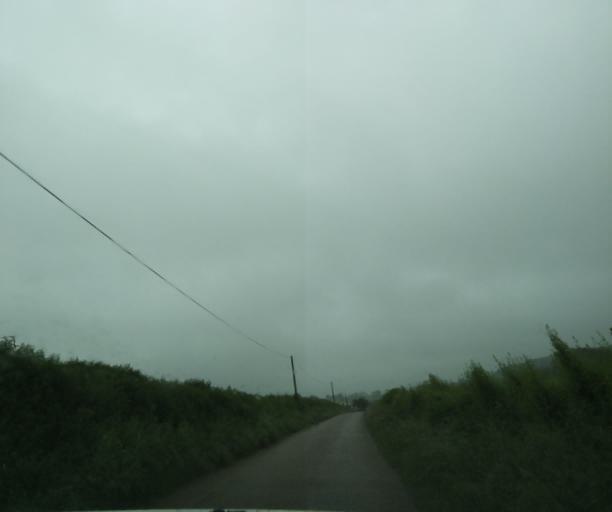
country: FR
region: Bourgogne
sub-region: Departement de Saone-et-Loire
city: Charolles
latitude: 46.3954
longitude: 4.2916
